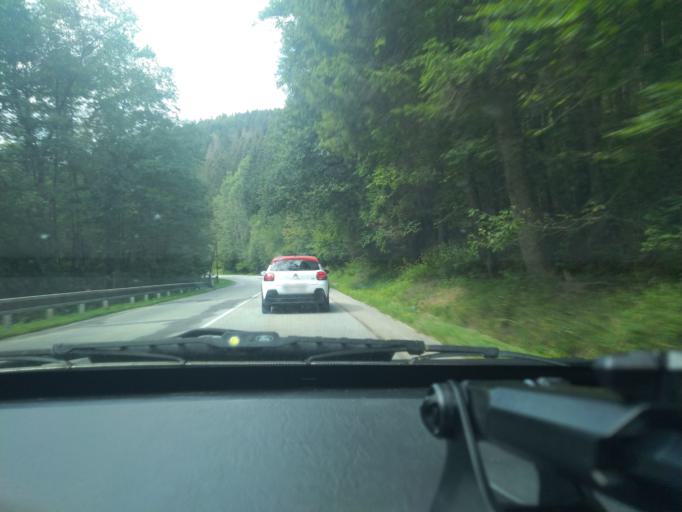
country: SK
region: Banskobystricky
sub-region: Okres Ziar nad Hronom
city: Kremnica
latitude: 48.8390
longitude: 18.9079
